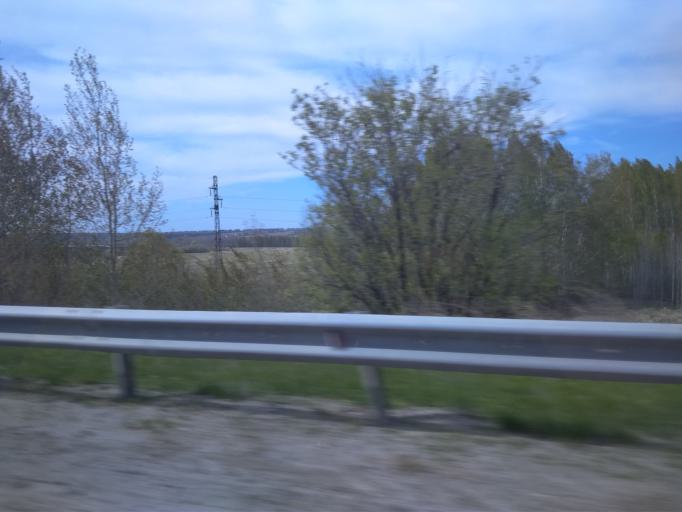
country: RU
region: Mordoviya
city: Chamzinka
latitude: 54.3633
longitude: 45.6172
